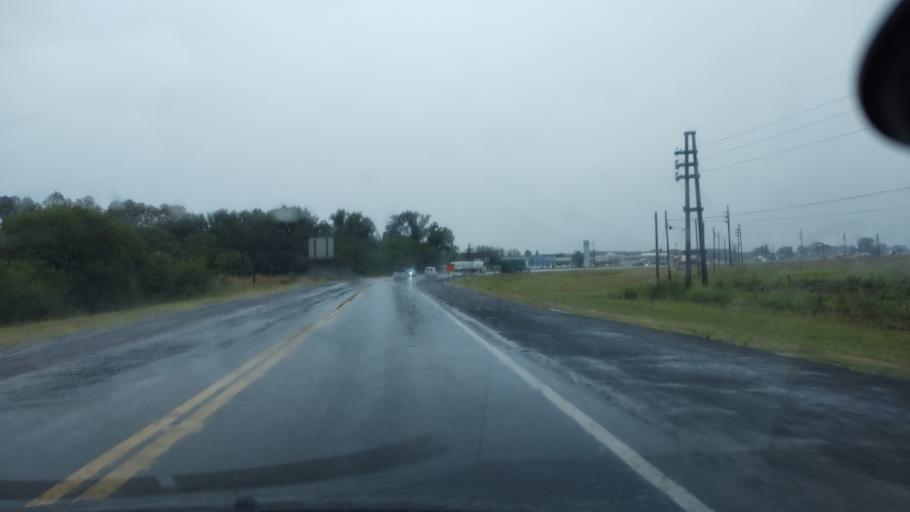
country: AR
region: Buenos Aires
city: Canuelas
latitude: -35.0249
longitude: -58.7462
